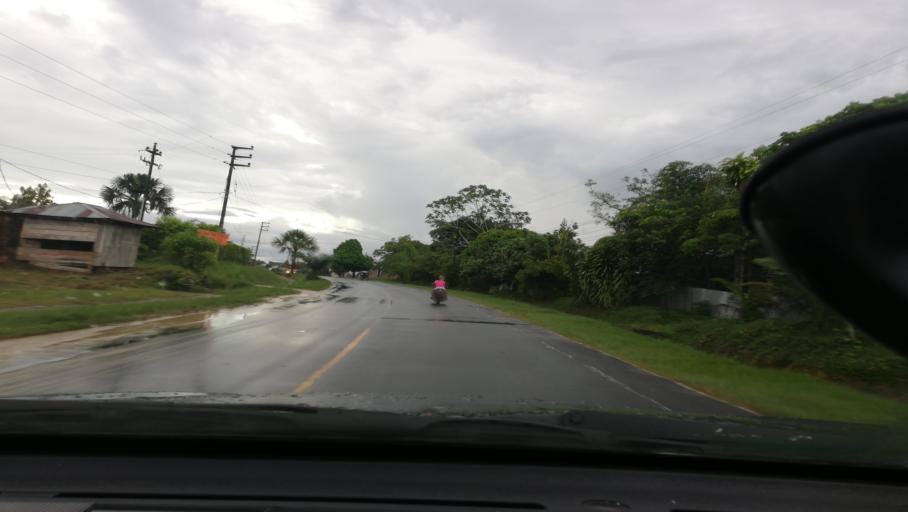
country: PE
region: Loreto
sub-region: Provincia de Maynas
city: Iquitos
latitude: -3.8425
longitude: -73.3344
